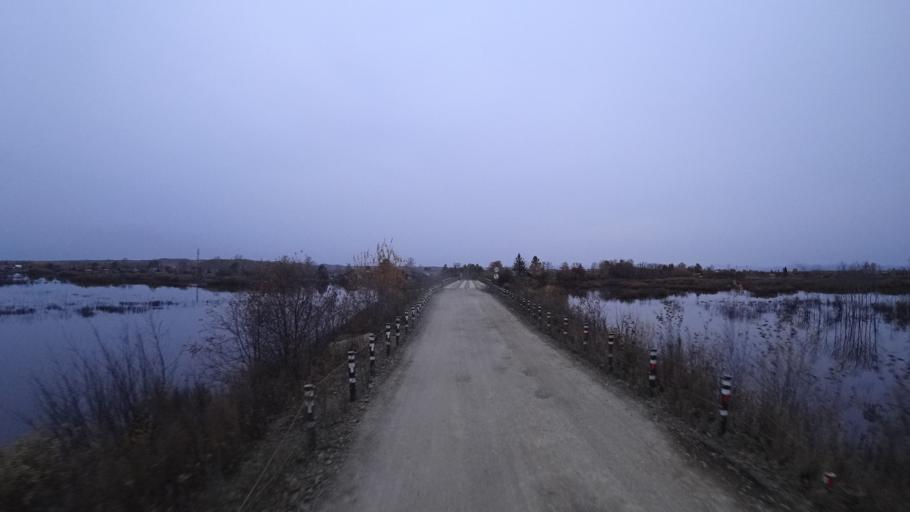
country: RU
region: Khabarovsk Krai
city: Amursk
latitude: 49.8973
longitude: 136.1443
